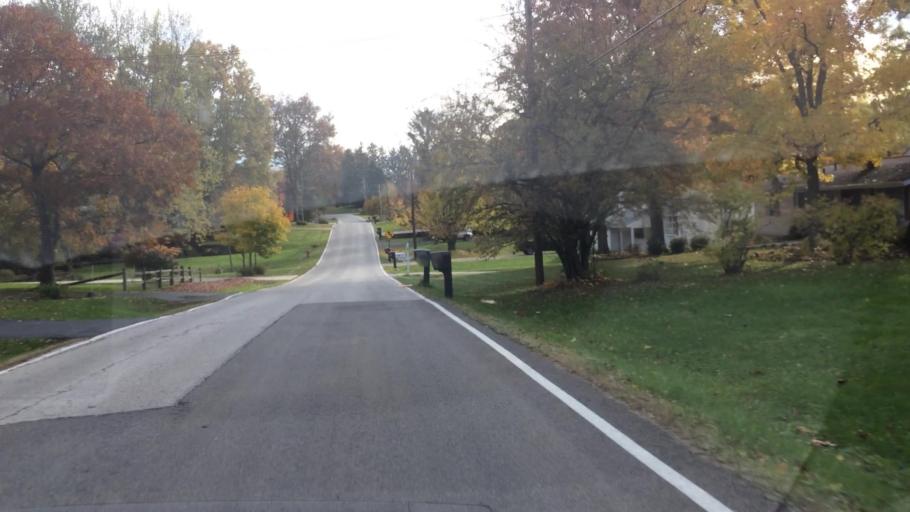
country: US
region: Ohio
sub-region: Summit County
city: Silver Lake
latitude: 41.1712
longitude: -81.4588
